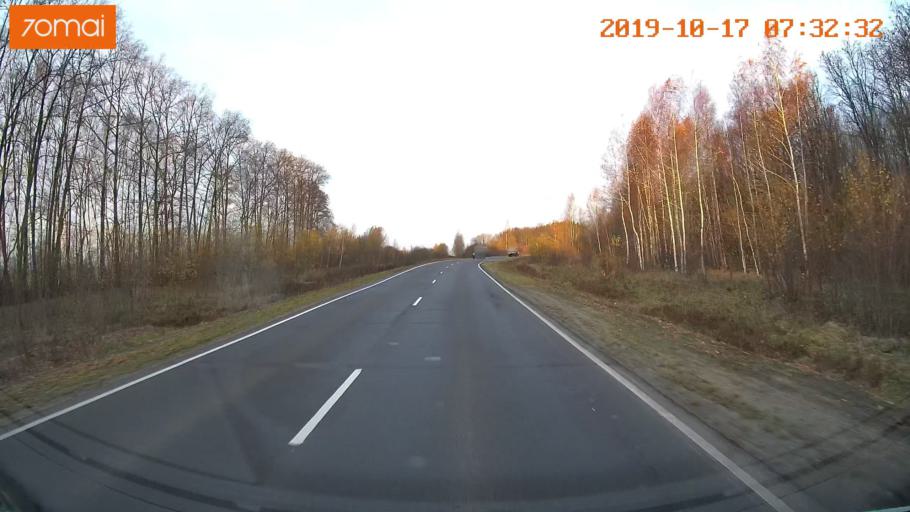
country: RU
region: Ivanovo
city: Gavrilov Posad
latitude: 56.3977
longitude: 39.9731
